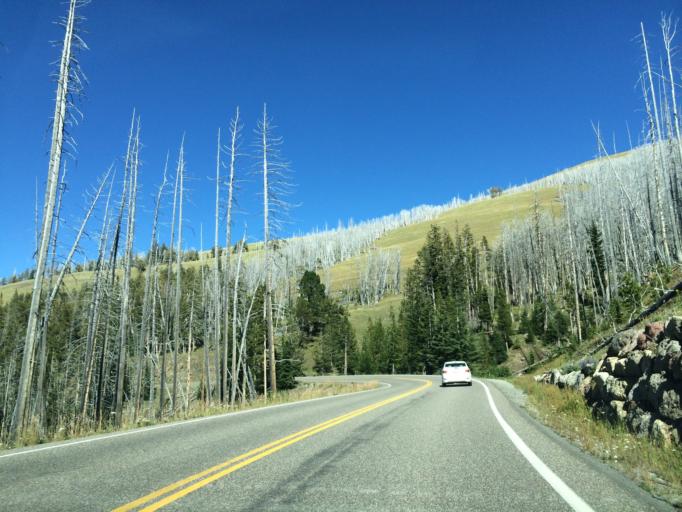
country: US
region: Montana
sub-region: Gallatin County
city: West Yellowstone
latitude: 44.8071
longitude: -110.4438
